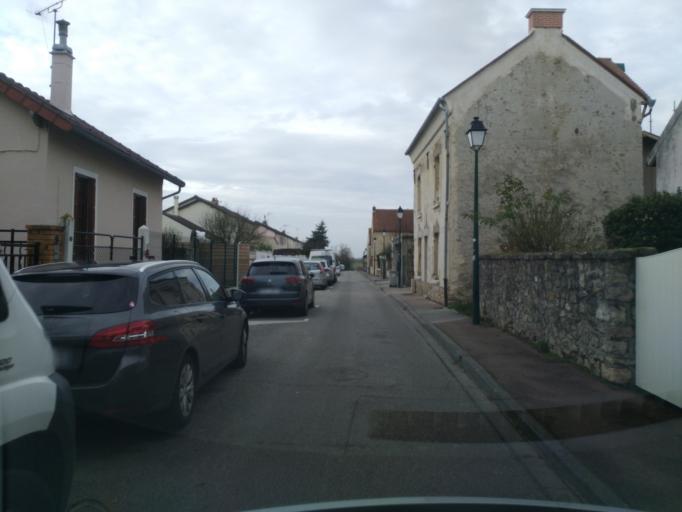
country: FR
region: Ile-de-France
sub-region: Departement des Yvelines
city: Fontenay-le-Fleury
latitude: 48.8171
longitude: 2.0451
